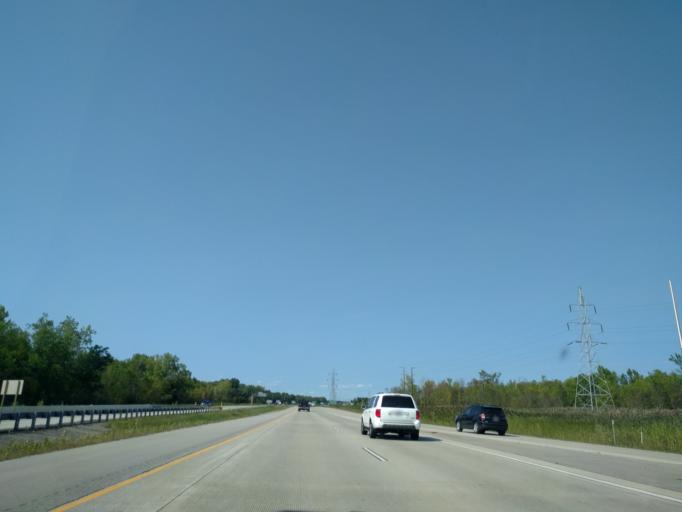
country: US
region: Wisconsin
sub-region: Brown County
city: Suamico
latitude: 44.5945
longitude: -88.0490
